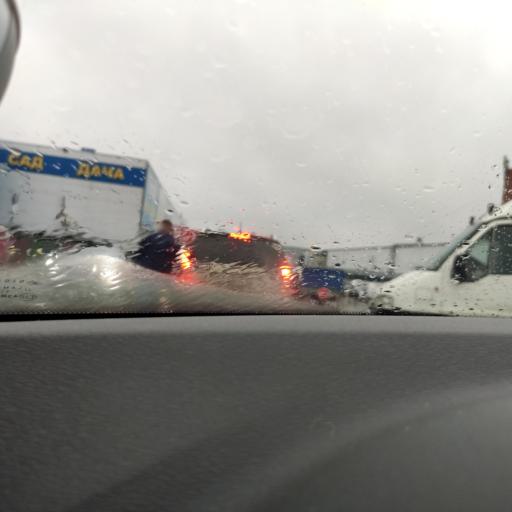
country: RU
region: Samara
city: Petra-Dubrava
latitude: 53.2776
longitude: 50.2727
